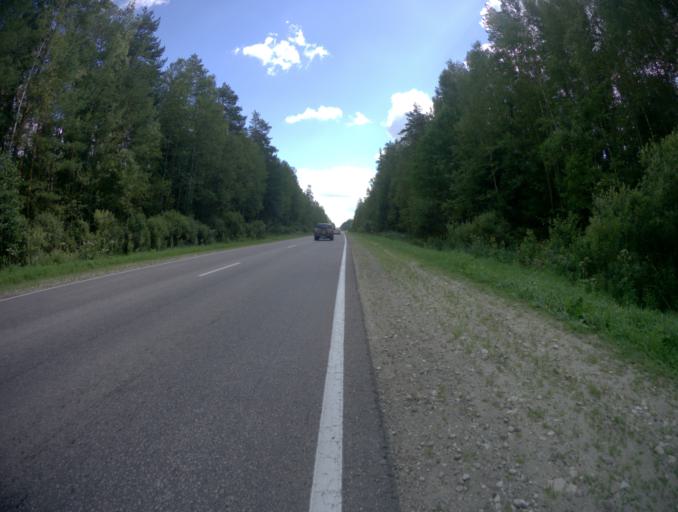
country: RU
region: Vladimir
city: Orgtrud
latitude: 56.0075
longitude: 40.6353
